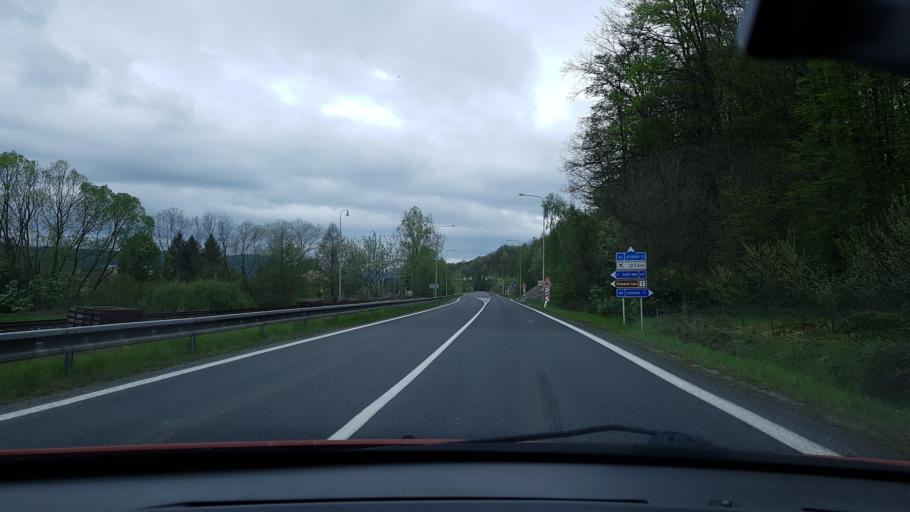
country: CZ
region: Olomoucky
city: Mikulovice
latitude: 50.3050
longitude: 17.3247
